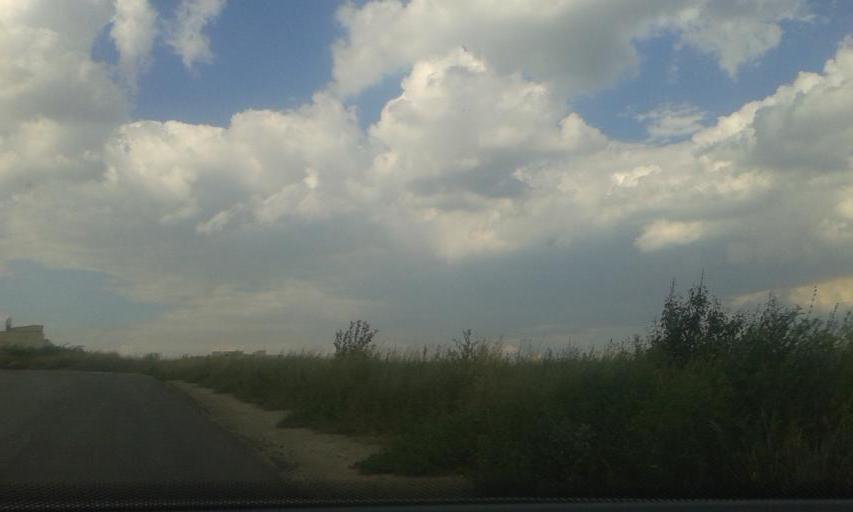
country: RU
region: Volgograd
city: Volgograd
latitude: 48.6385
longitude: 44.4223
